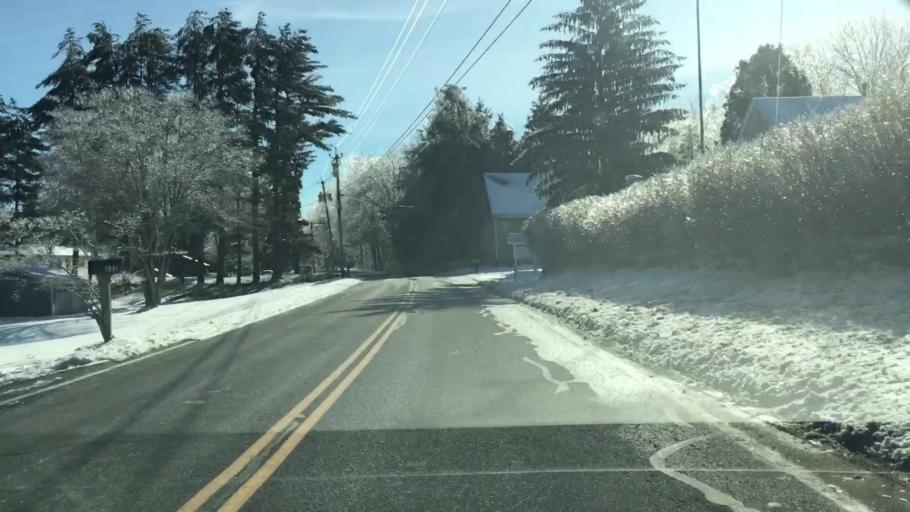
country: US
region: Connecticut
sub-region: Fairfield County
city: Newtown
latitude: 41.3620
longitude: -73.2400
